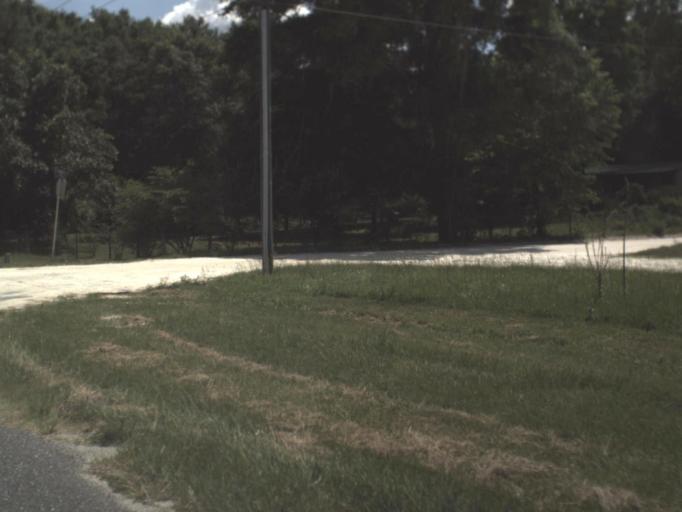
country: US
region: Florida
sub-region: Alachua County
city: High Springs
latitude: 29.9021
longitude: -82.6094
